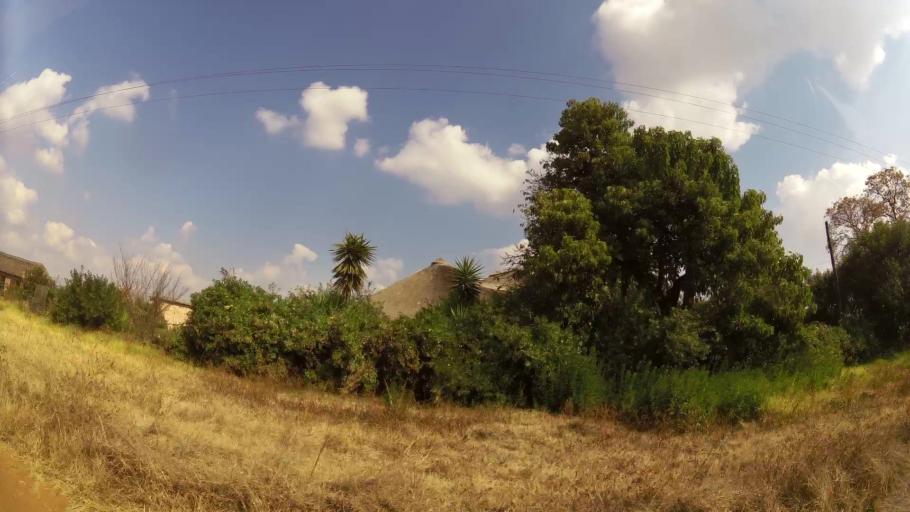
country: ZA
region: Mpumalanga
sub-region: Nkangala District Municipality
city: Delmas
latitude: -26.1499
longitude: 28.5457
